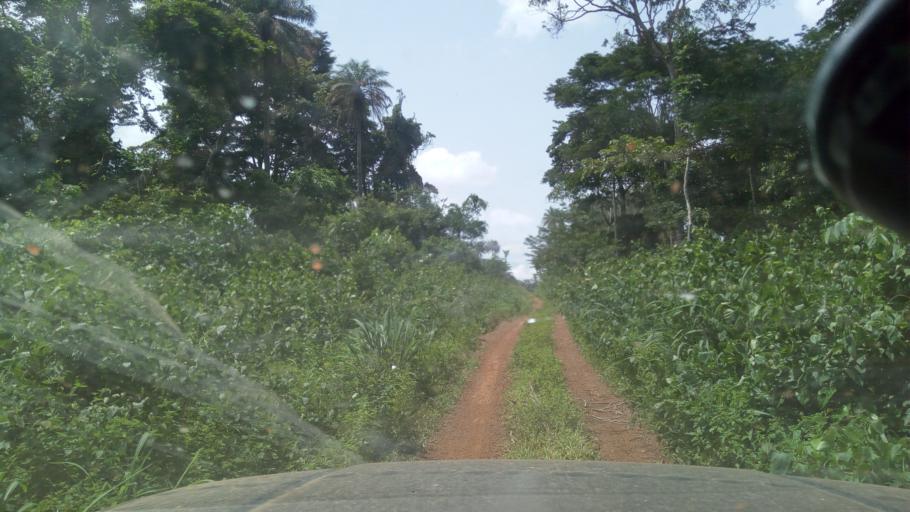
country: SL
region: Eastern Province
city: Segbwema
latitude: 7.9747
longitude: -11.0176
